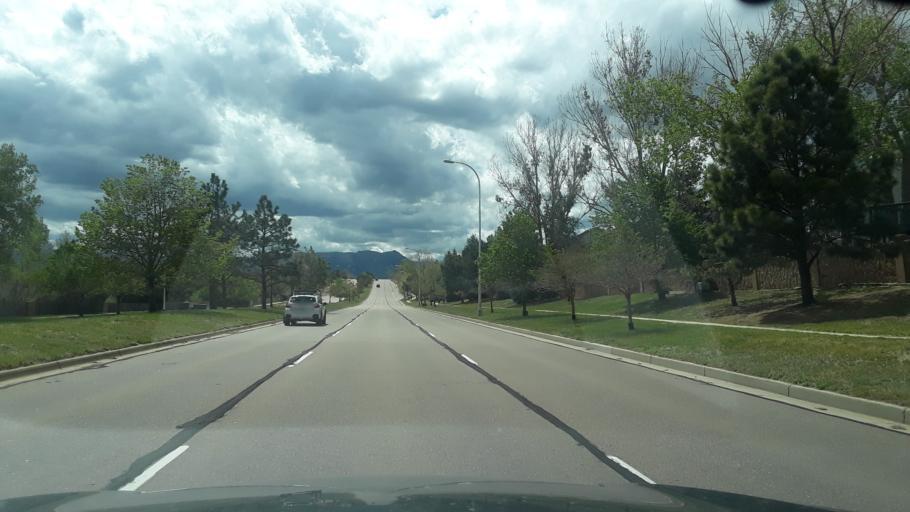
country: US
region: Colorado
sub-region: El Paso County
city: Black Forest
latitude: 38.9569
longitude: -104.7521
